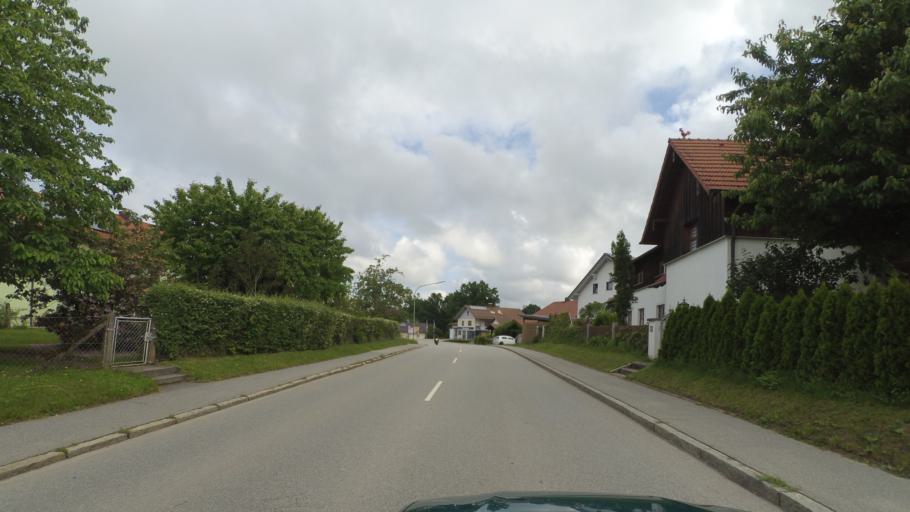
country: DE
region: Bavaria
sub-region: Lower Bavaria
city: Mitterfels
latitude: 48.9805
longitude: 12.6820
